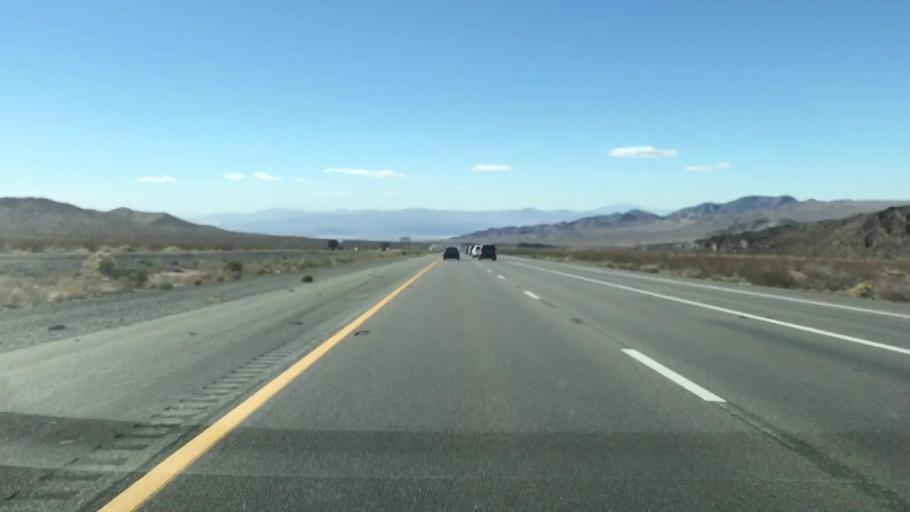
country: US
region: Nevada
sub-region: Clark County
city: Sandy Valley
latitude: 35.3829
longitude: -115.8651
